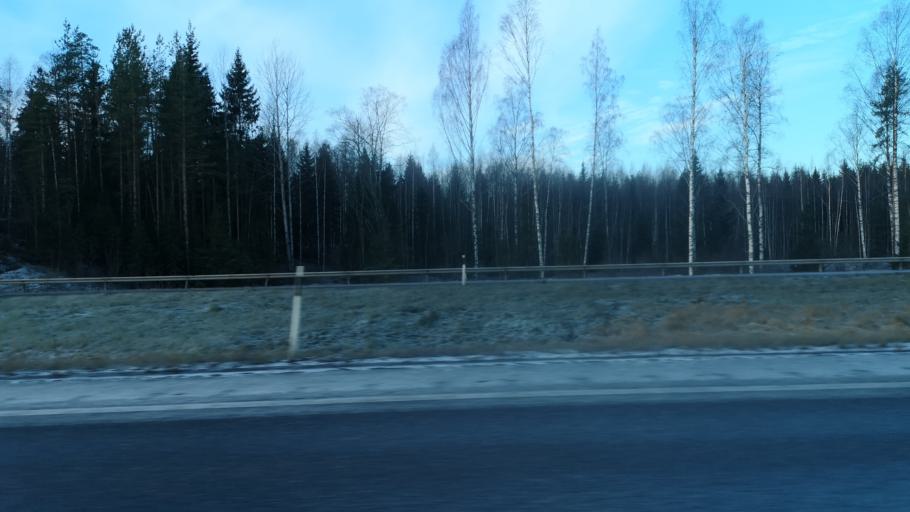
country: FI
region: Uusimaa
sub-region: Helsinki
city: Kerava
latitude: 60.4324
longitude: 25.1258
